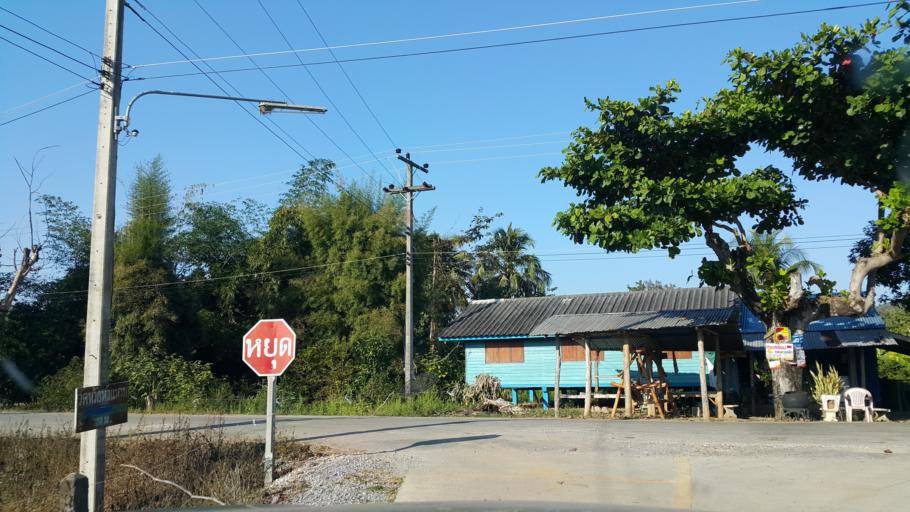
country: TH
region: Sukhothai
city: Thung Saliam
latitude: 17.3818
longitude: 99.5231
